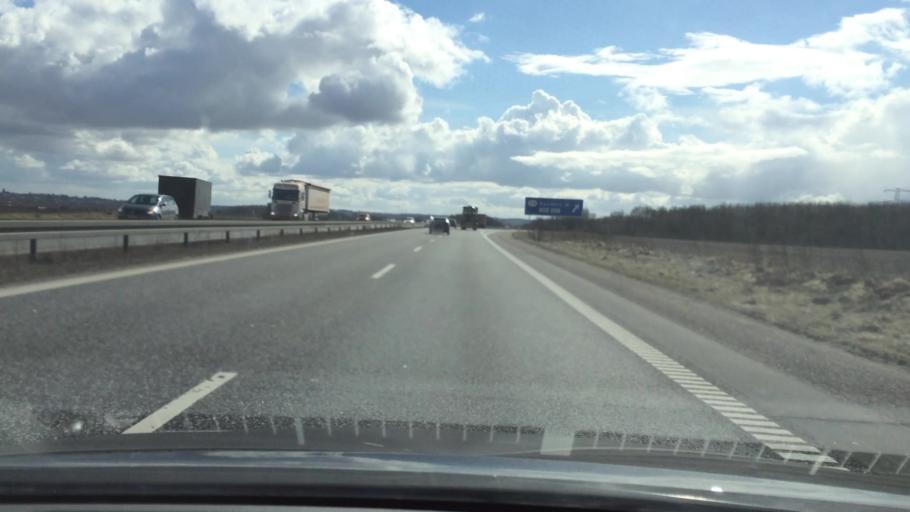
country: DK
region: Central Jutland
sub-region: Randers Kommune
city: Randers
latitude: 56.4975
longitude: 9.9786
